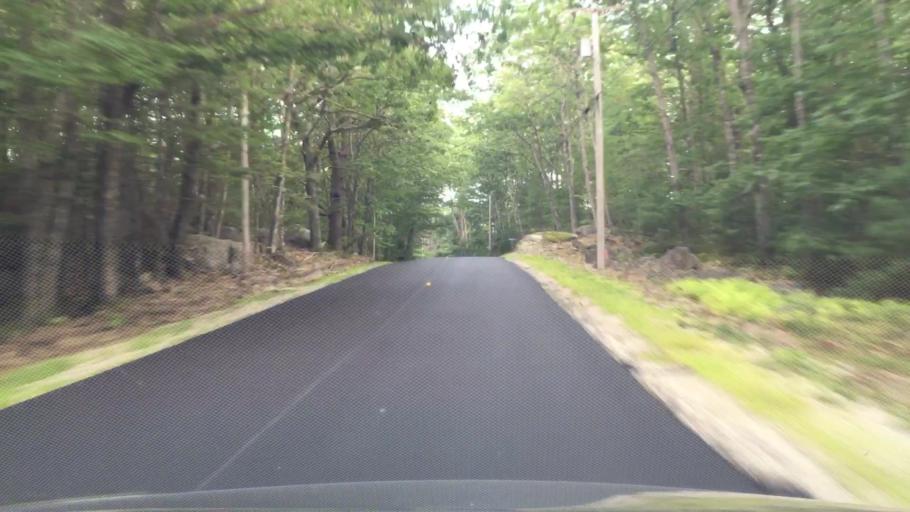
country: US
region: Maine
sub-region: Hancock County
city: Surry
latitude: 44.5204
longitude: -68.6080
